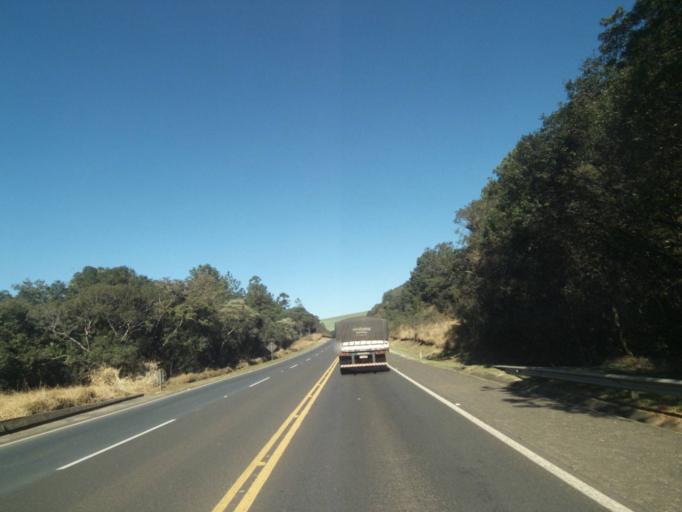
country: BR
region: Parana
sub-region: Reserva
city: Reserva
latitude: -24.6482
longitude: -50.6217
